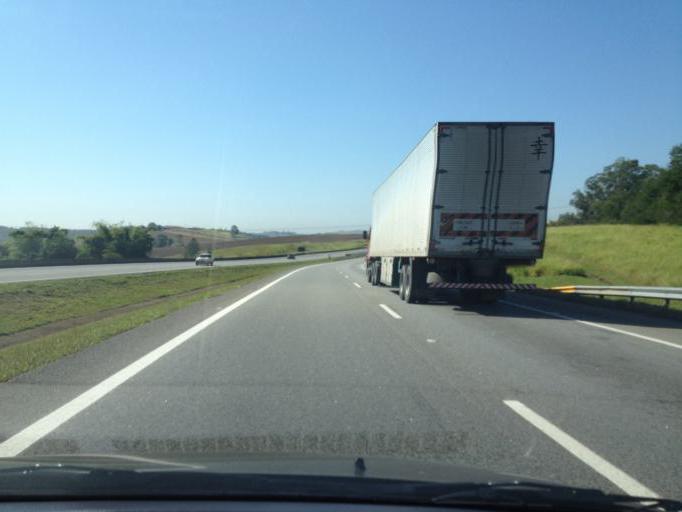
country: BR
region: Sao Paulo
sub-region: Guararema
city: Guararema
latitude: -23.3592
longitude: -46.0944
